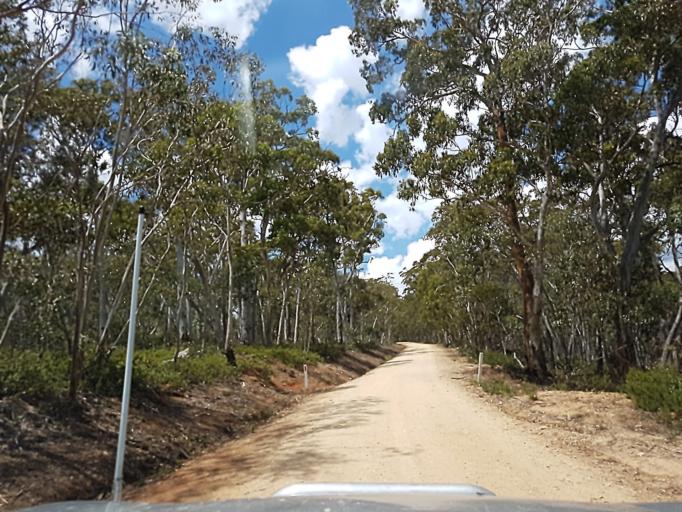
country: AU
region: New South Wales
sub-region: Snowy River
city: Jindabyne
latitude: -36.9019
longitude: 148.0992
